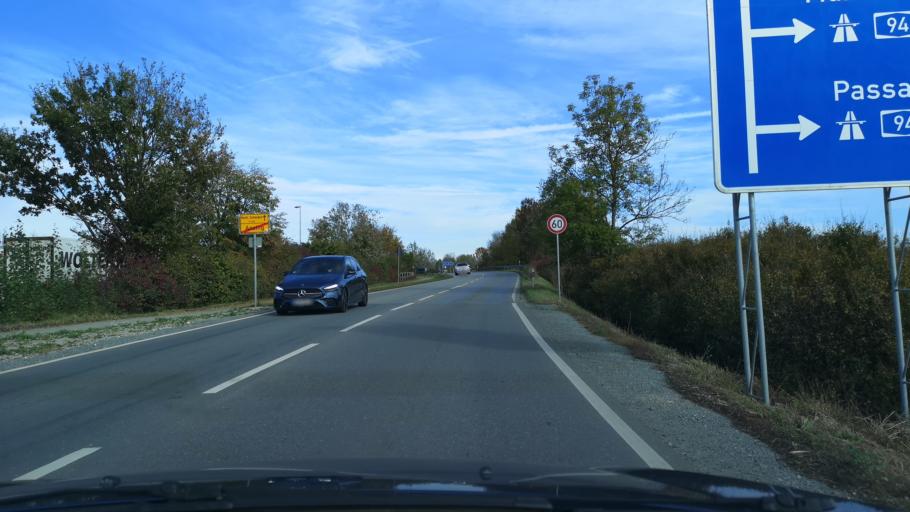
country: DE
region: Bavaria
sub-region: Upper Bavaria
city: Anzing
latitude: 48.1592
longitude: 11.8544
